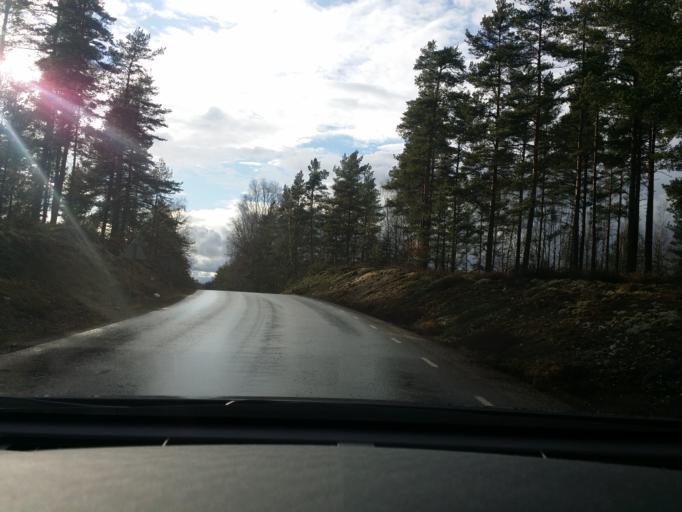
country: SE
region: Soedermanland
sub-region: Eskilstuna Kommun
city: Arla
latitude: 59.3253
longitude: 16.6789
